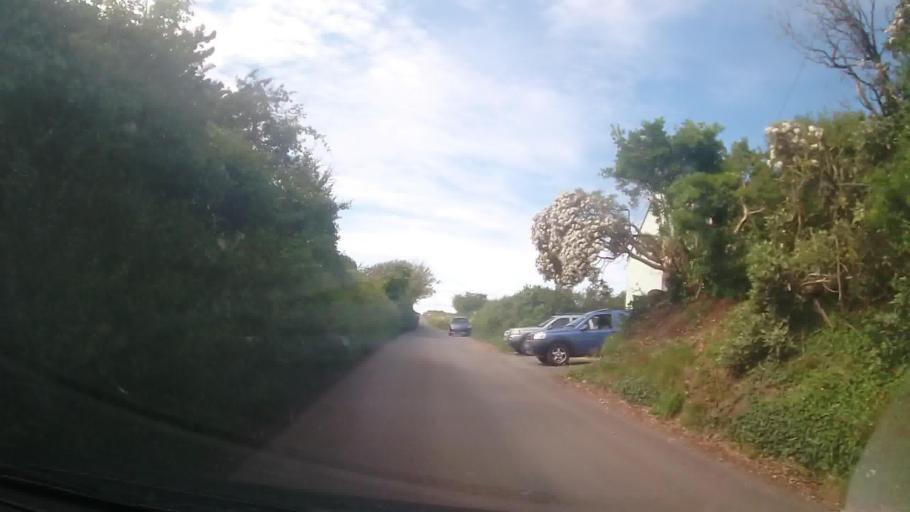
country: GB
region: England
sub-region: Devon
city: Salcombe
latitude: 50.2438
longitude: -3.6807
